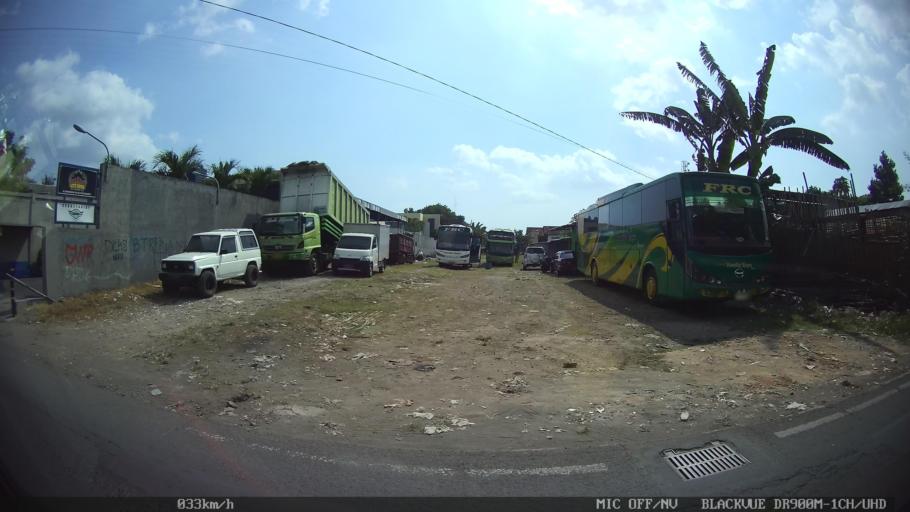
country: ID
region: Daerah Istimewa Yogyakarta
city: Yogyakarta
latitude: -7.8199
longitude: 110.3906
